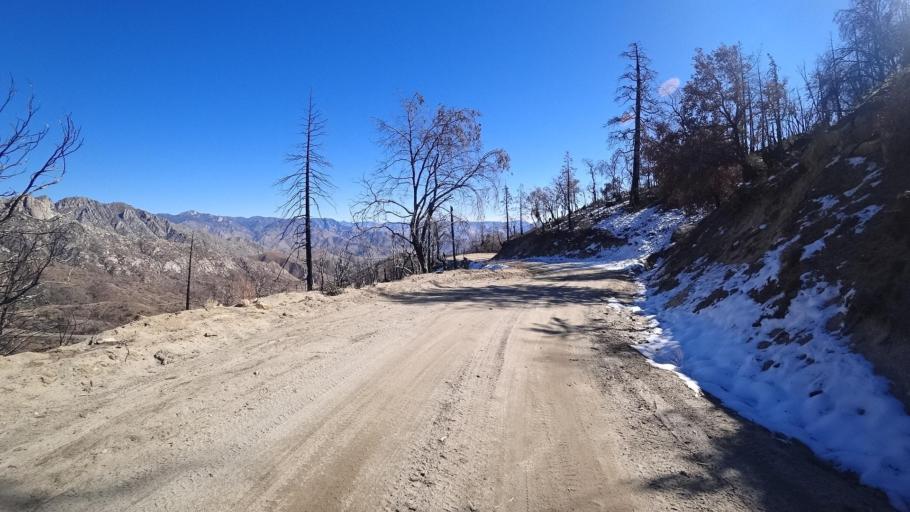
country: US
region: California
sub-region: Kern County
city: Alta Sierra
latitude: 35.7184
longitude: -118.5291
